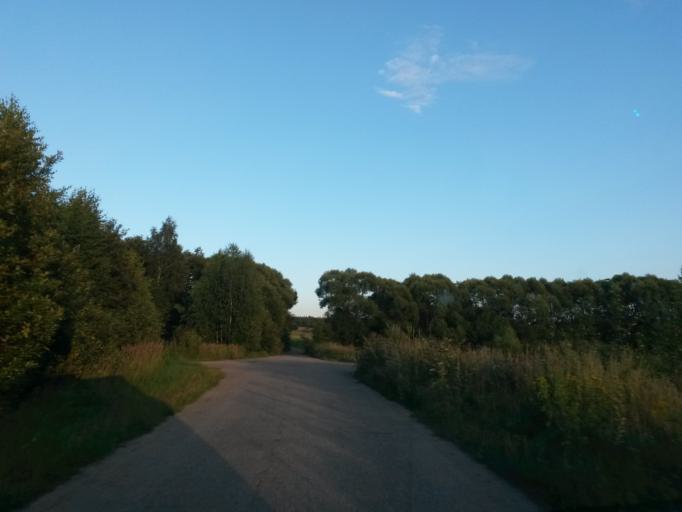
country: RU
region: Jaroslavl
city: Gavrilov-Yam
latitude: 57.3372
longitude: 40.0383
